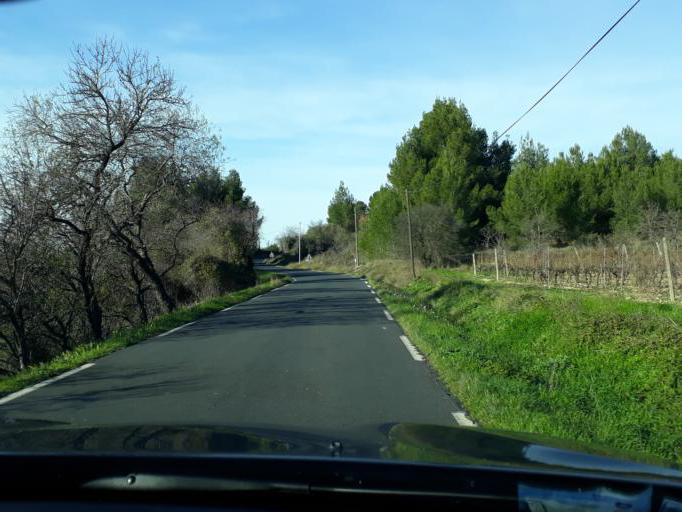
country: FR
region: Languedoc-Roussillon
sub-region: Departement de l'Herault
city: Castelnau-de-Guers
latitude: 43.4175
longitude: 3.4322
